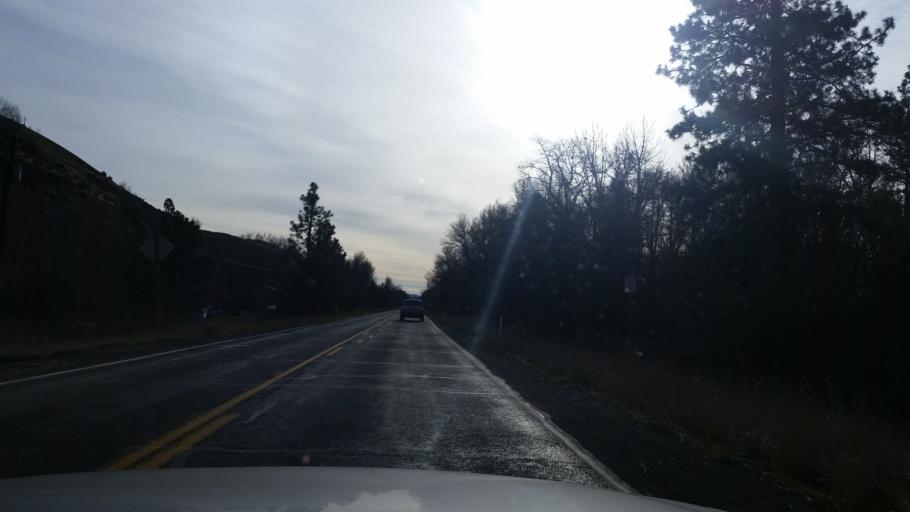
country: US
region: Washington
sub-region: Kittitas County
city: Ellensburg
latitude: 47.0695
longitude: -120.6556
